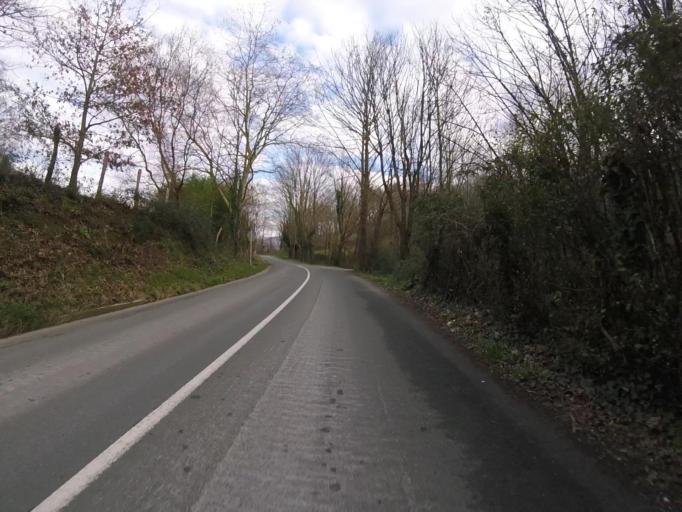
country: ES
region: Basque Country
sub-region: Provincia de Guipuzcoa
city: Irun
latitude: 43.3200
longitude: -1.8207
